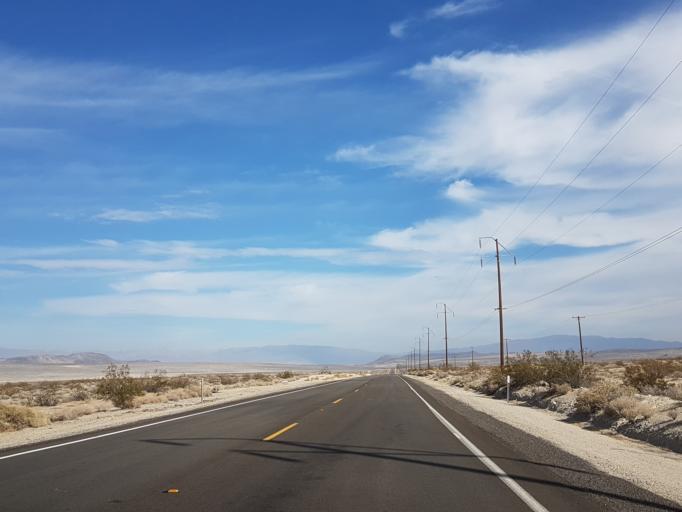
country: US
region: California
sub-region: Kern County
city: Ridgecrest
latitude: 35.6437
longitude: -117.5400
